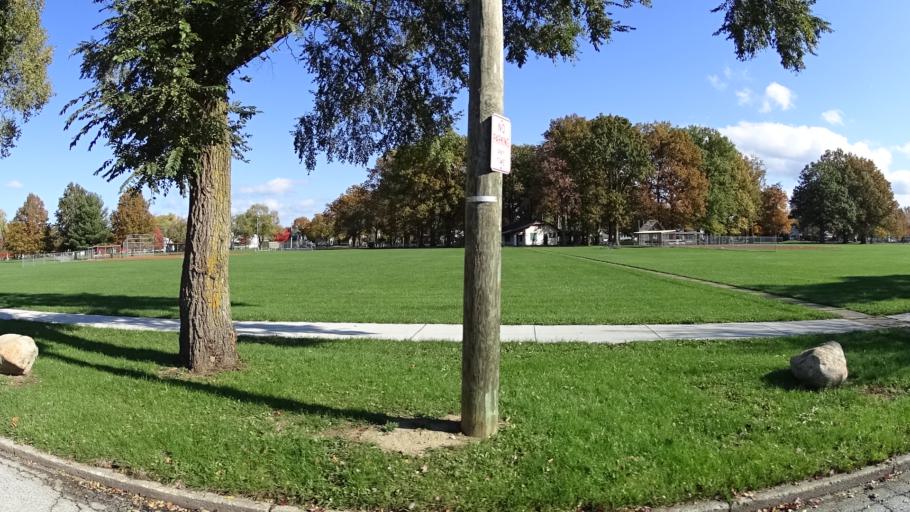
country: US
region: Ohio
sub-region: Lorain County
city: Lorain
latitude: 41.4603
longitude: -82.1959
